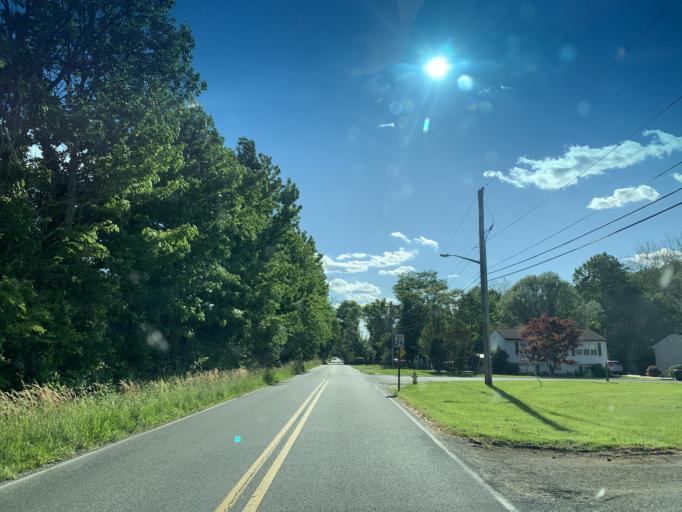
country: US
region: Maryland
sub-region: Cecil County
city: Perryville
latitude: 39.5739
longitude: -76.0705
